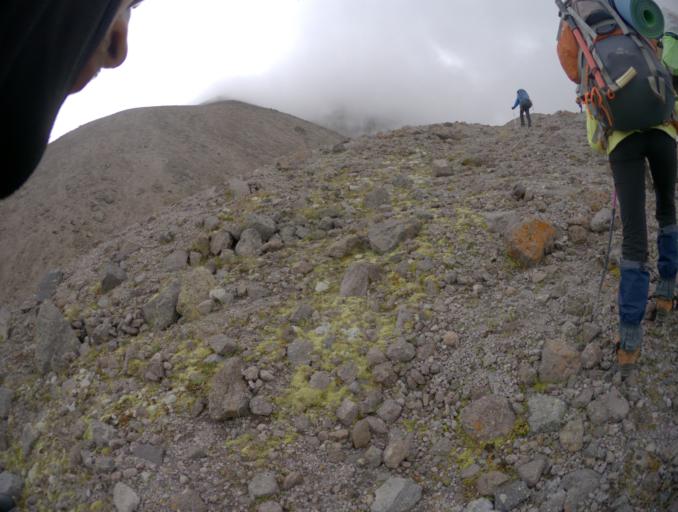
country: RU
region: Kabardino-Balkariya
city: Terskol
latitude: 43.3824
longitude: 42.3827
